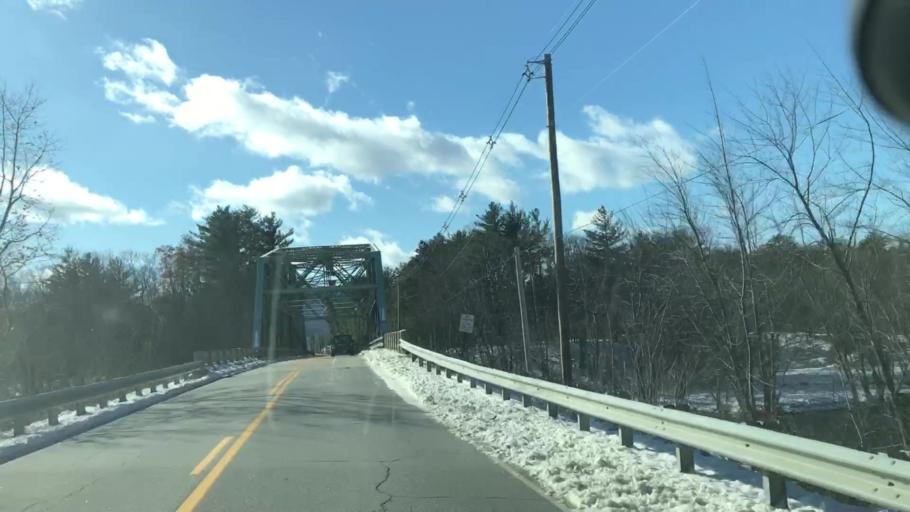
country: US
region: Maine
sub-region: Oxford County
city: Brownfield
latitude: 43.9561
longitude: -70.8818
